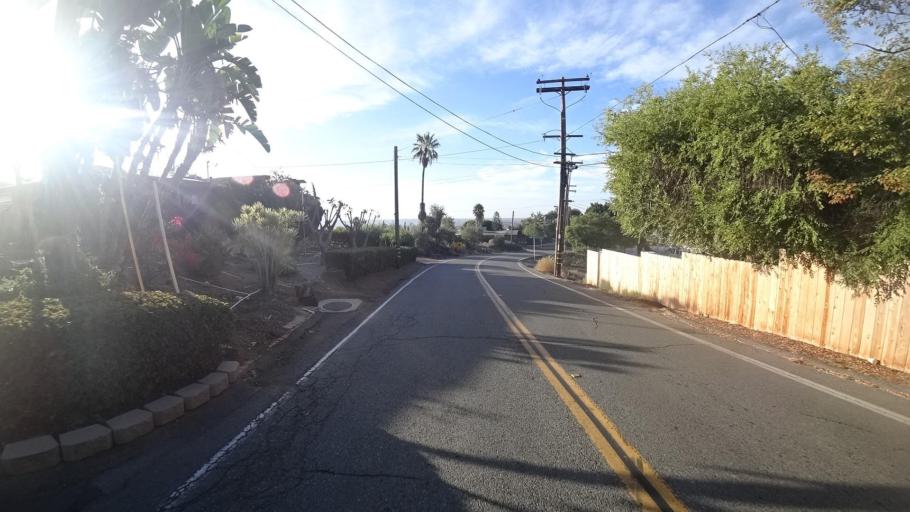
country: US
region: California
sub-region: San Diego County
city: La Presa
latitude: 32.7210
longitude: -117.0087
